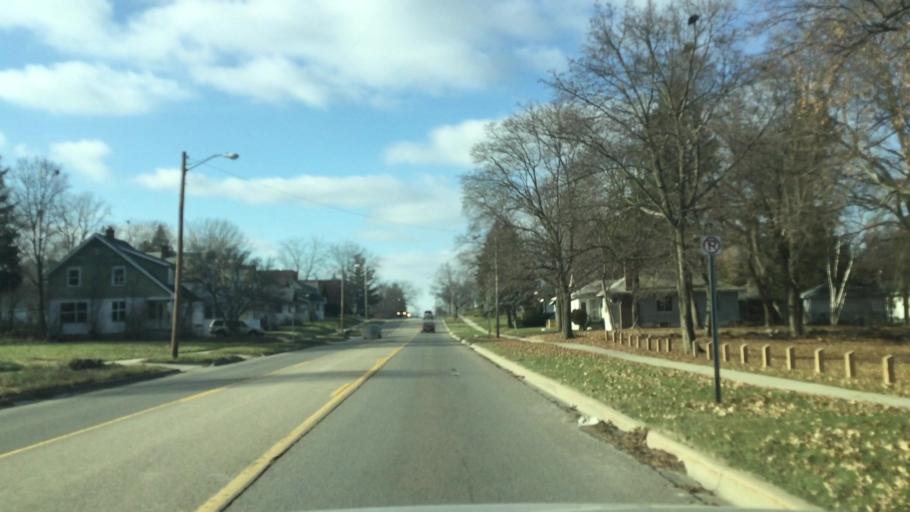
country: US
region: Michigan
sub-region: Genesee County
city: Flint
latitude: 43.0199
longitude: -83.7150
